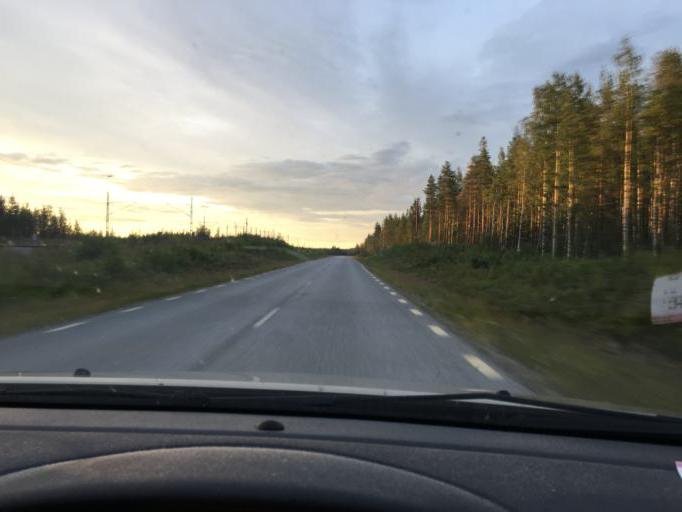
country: SE
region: Norrbotten
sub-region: Lulea Kommun
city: Ranea
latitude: 66.0438
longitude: 22.3424
